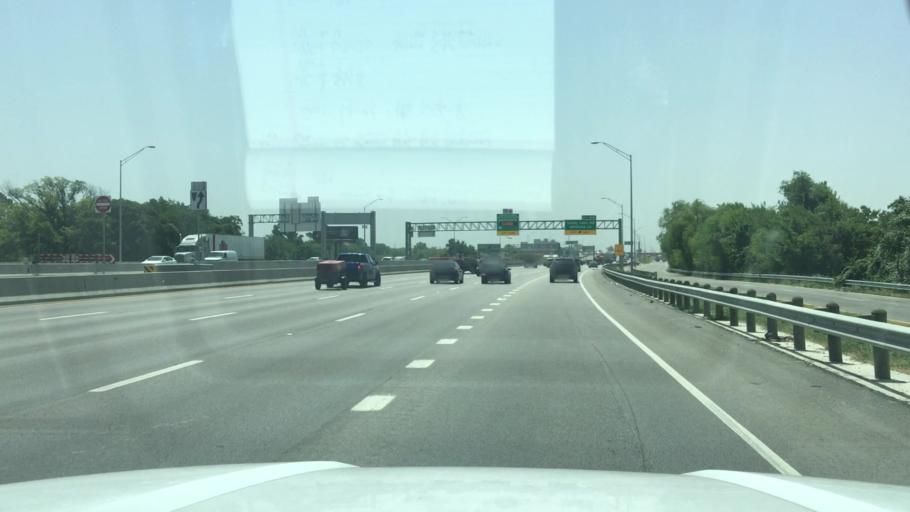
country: US
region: Texas
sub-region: Dallas County
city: Carrollton
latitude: 32.9740
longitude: -96.9230
